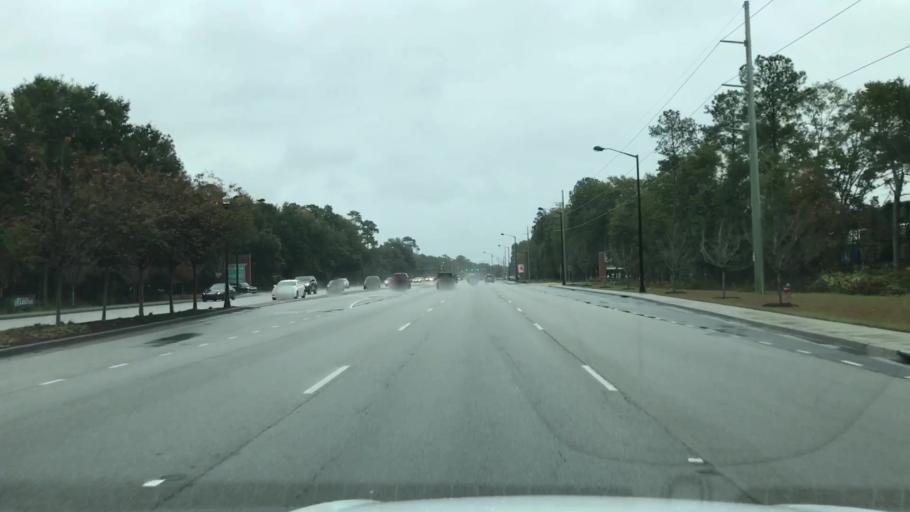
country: US
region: South Carolina
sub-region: Charleston County
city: Isle of Palms
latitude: 32.8696
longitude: -79.7796
